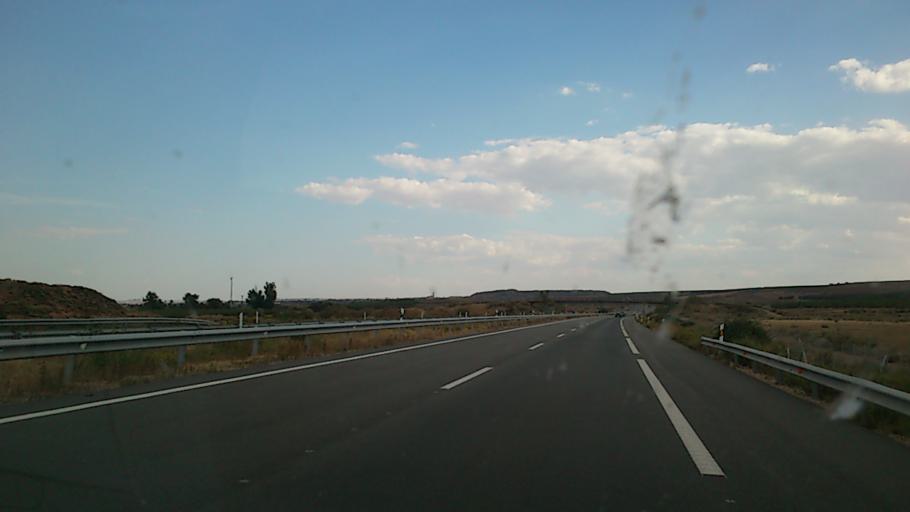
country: ES
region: Navarre
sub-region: Provincia de Navarra
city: Azagra
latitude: 42.2703
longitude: -1.9309
